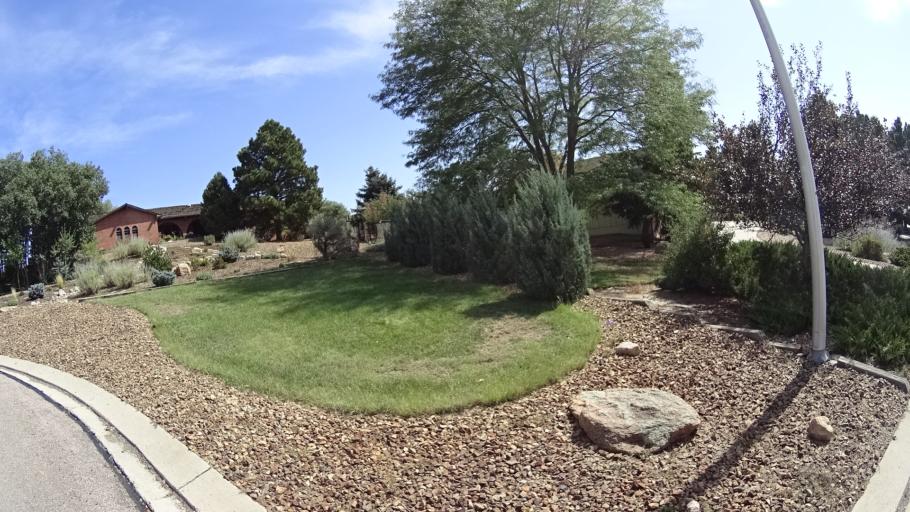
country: US
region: Colorado
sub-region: El Paso County
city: Cimarron Hills
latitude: 38.9106
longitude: -104.7589
